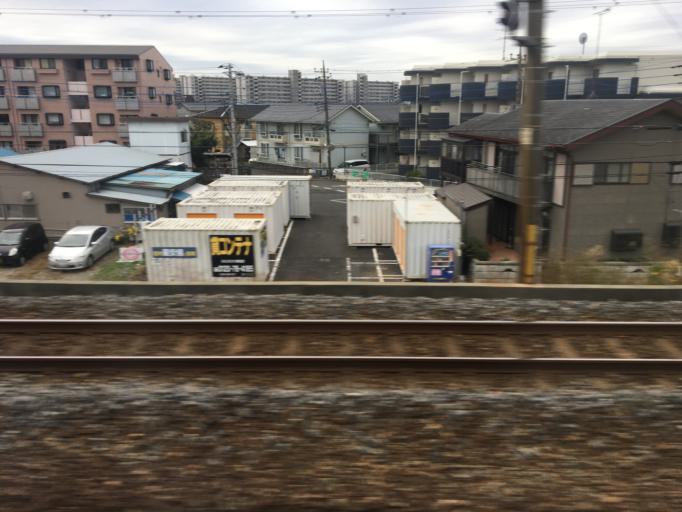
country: JP
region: Chiba
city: Nagareyama
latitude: 35.8346
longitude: 139.9072
